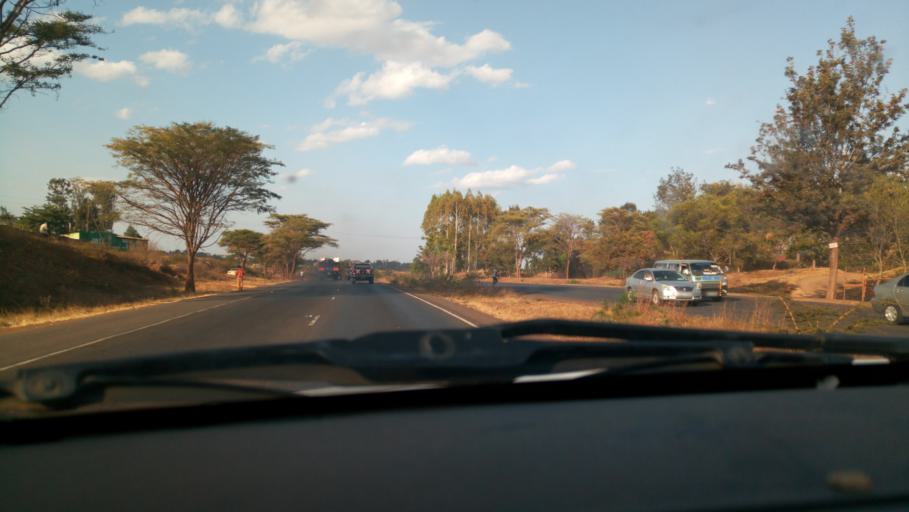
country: KE
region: Nairobi Area
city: Thika
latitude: -0.9577
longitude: 37.1113
